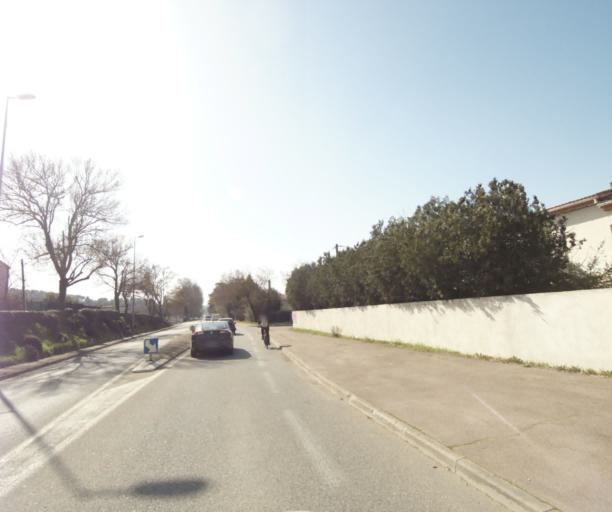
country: FR
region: Provence-Alpes-Cote d'Azur
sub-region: Departement des Bouches-du-Rhone
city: Bouc-Bel-Air
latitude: 43.4581
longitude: 5.4042
